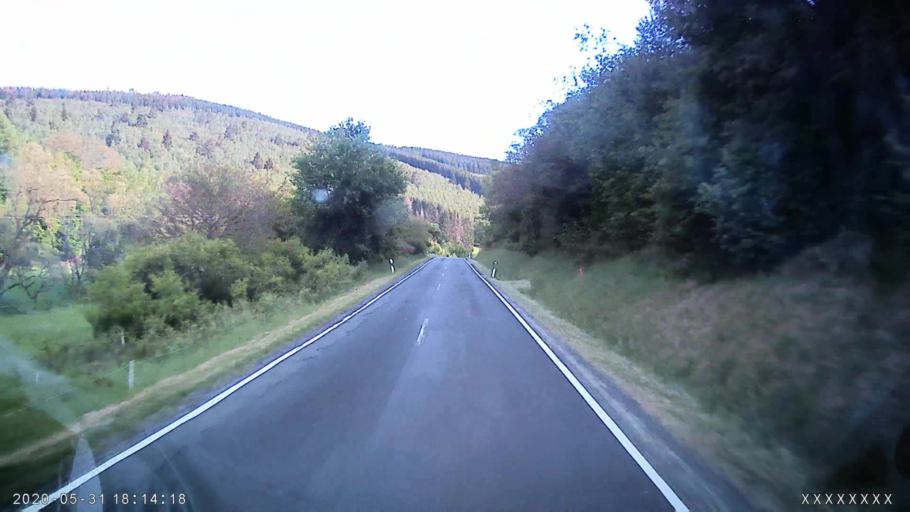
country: DE
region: Hesse
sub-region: Regierungsbezirk Giessen
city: Haiger
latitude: 50.8200
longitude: 8.2212
